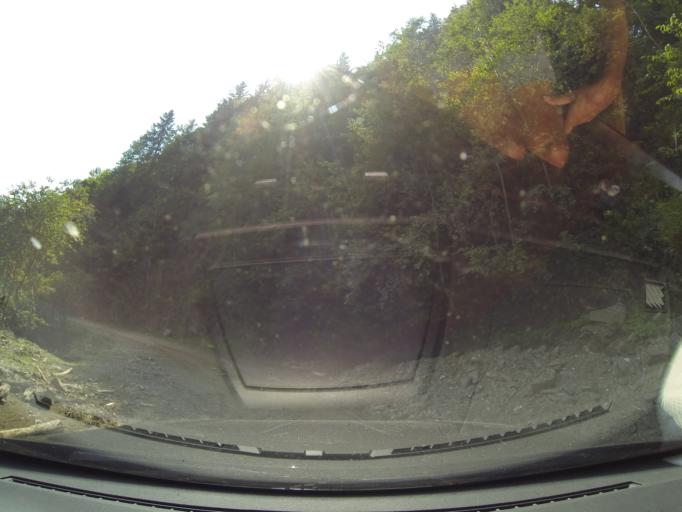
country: RO
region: Arges
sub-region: Comuna Arefu
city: Arefu
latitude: 45.4771
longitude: 24.6309
